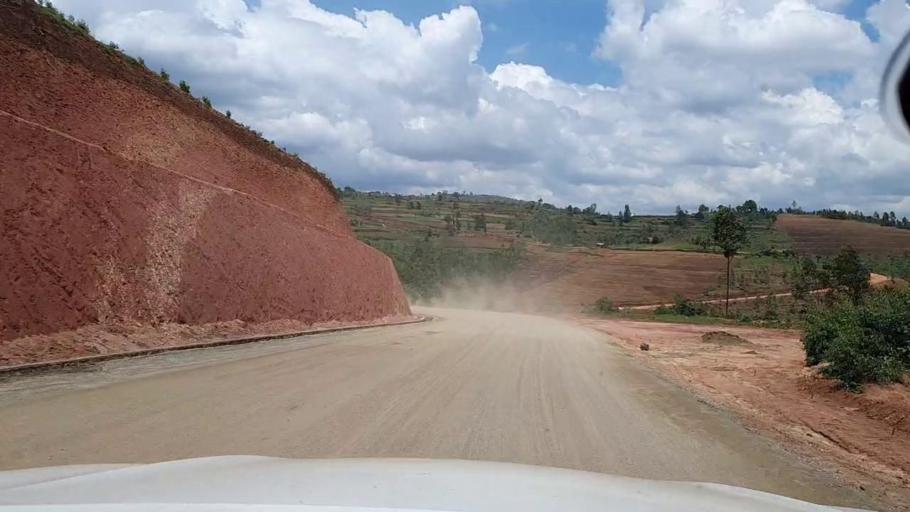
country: RW
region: Southern Province
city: Butare
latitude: -2.6946
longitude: 29.5565
